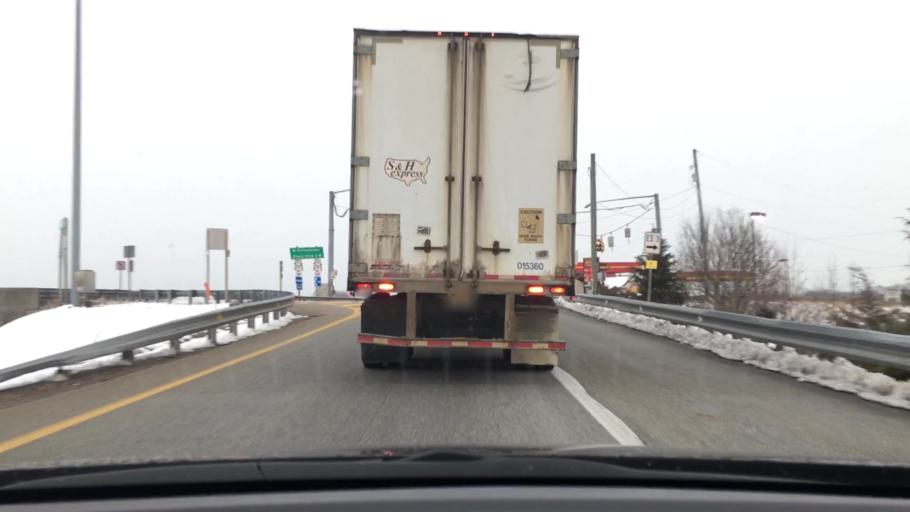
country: US
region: Pennsylvania
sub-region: York County
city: Manchester
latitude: 40.0823
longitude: -76.7658
